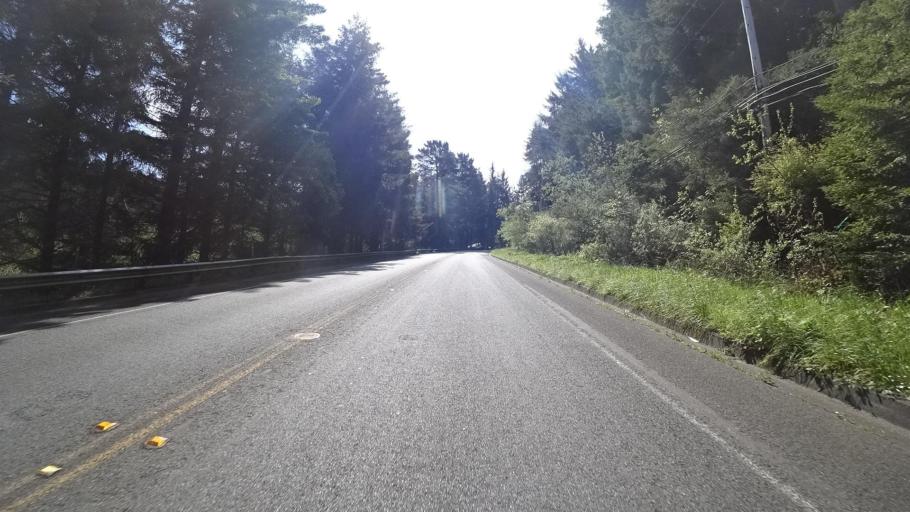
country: US
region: California
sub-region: Humboldt County
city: Cutten
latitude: 40.7673
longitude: -124.1561
